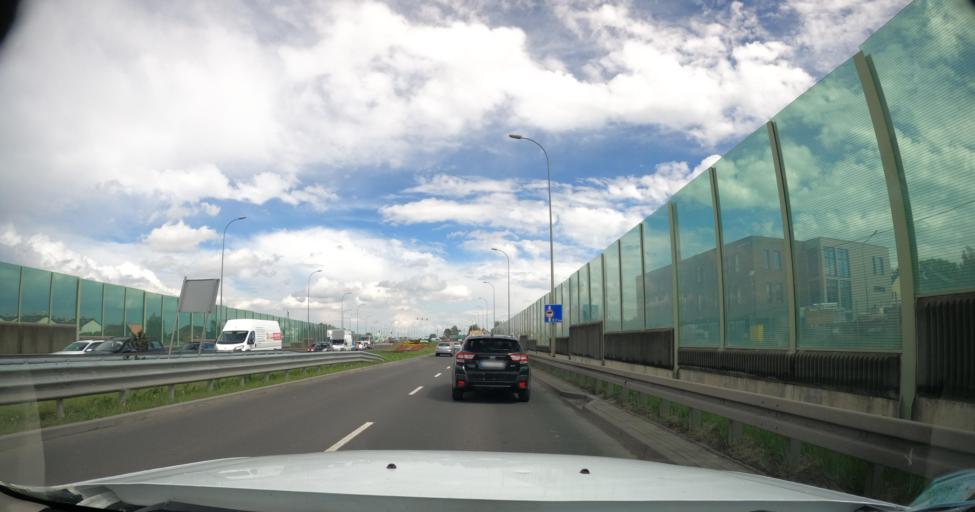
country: PL
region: Pomeranian Voivodeship
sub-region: Powiat gdanski
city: Lublewo Gdanskie
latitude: 54.3504
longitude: 18.5075
